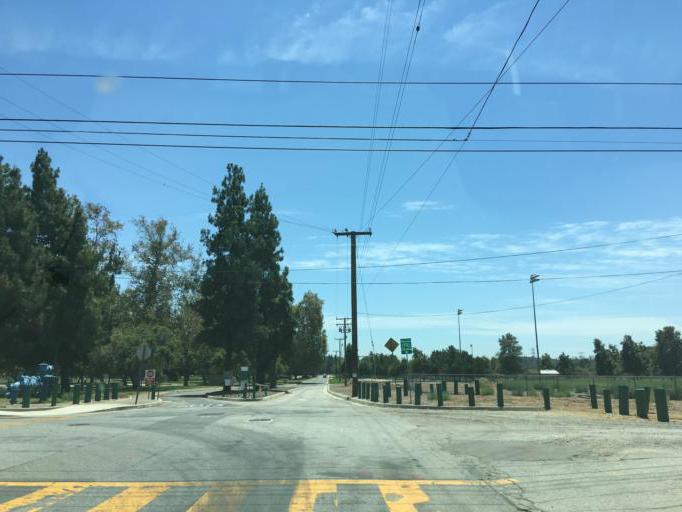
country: US
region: California
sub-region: Los Angeles County
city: South El Monte
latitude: 34.0520
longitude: -118.0688
